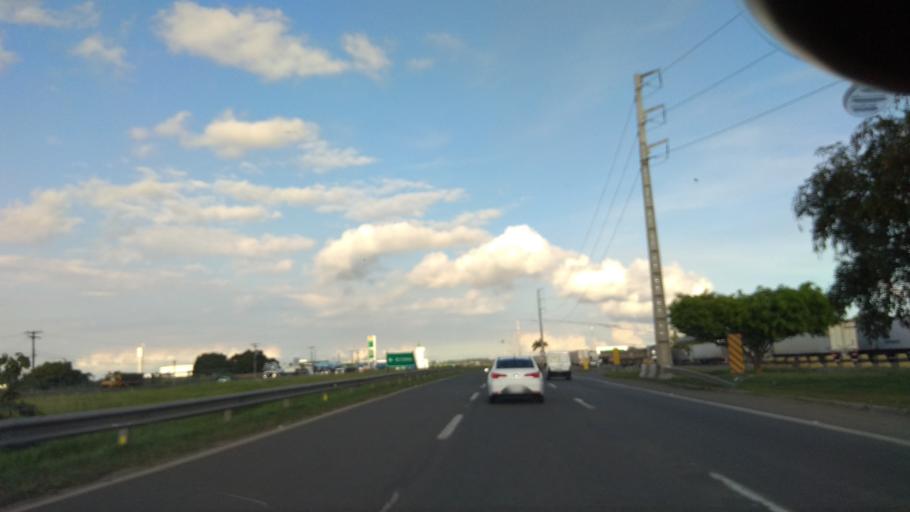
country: BR
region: Bahia
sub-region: Conceicao Do Jacuipe
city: Conceicao do Jacuipe
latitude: -12.3384
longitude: -38.8484
